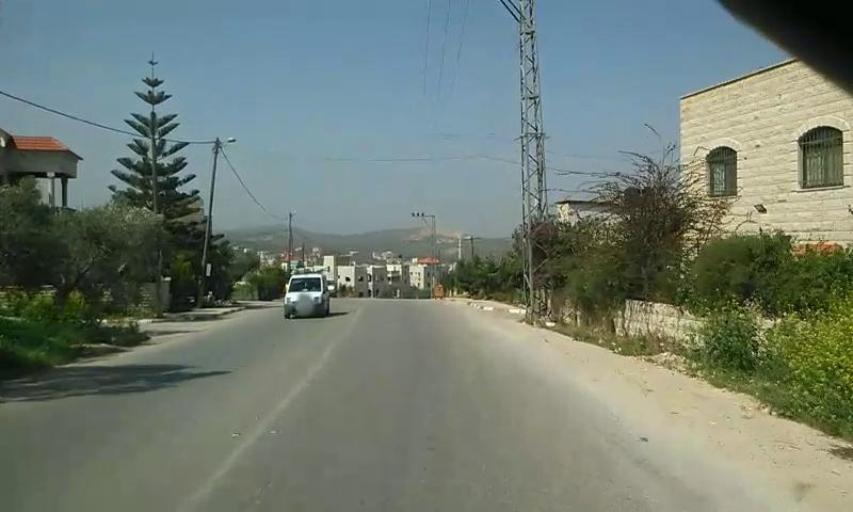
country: PS
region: West Bank
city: Az Zababidah
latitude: 32.3813
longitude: 35.3295
